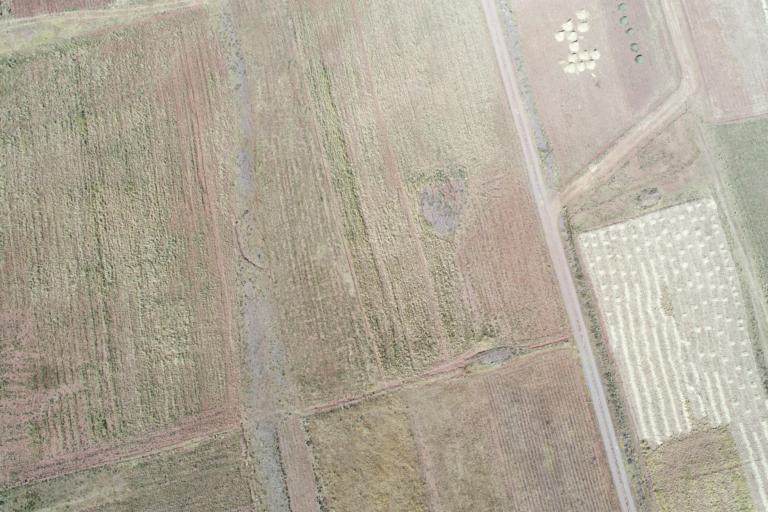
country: BO
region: La Paz
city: Tiahuanaco
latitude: -16.5974
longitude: -68.7814
